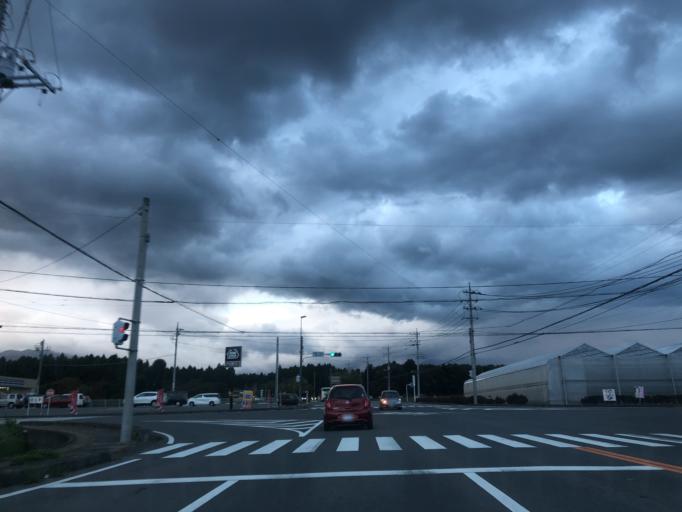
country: JP
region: Tochigi
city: Kuroiso
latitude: 36.9544
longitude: 140.0034
